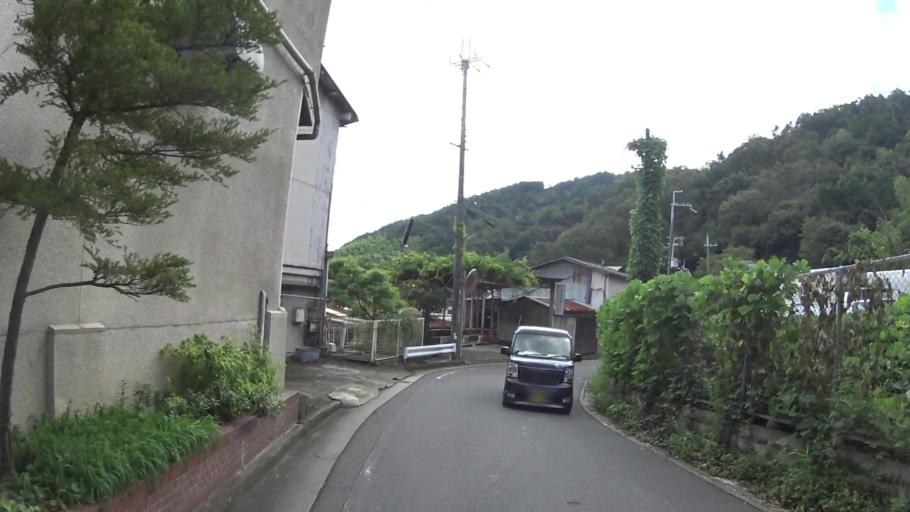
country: JP
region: Kyoto
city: Kyoto
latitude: 34.9749
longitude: 135.7914
